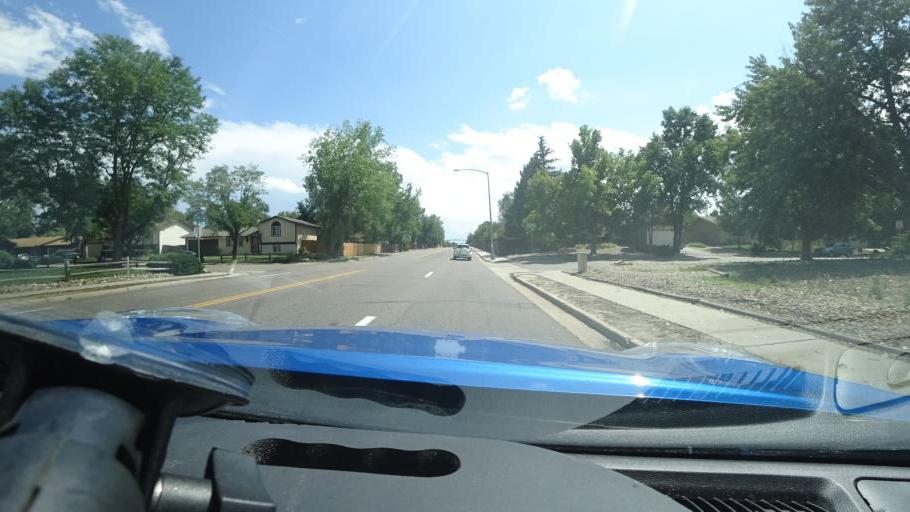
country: US
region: Colorado
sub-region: Adams County
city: Aurora
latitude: 39.6884
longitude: -104.8472
